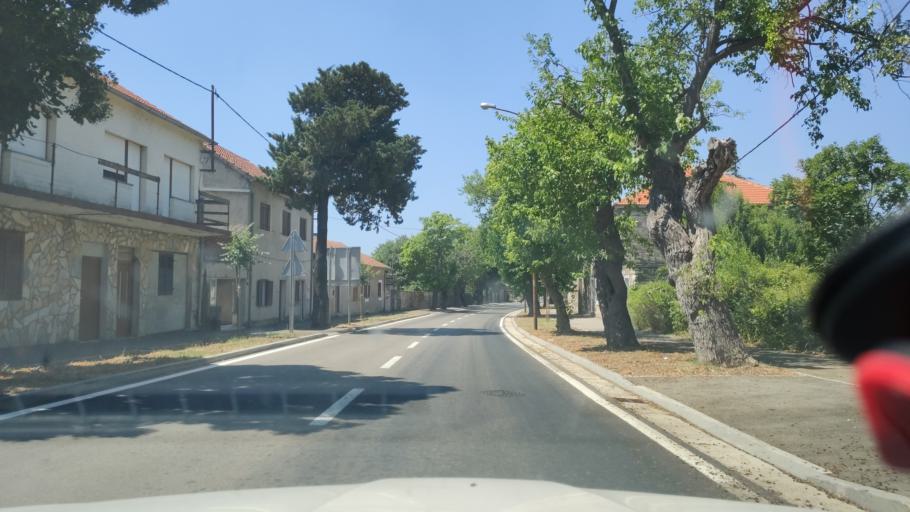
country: HR
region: Sibensko-Kniniska
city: Kistanje
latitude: 43.9799
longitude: 15.9593
